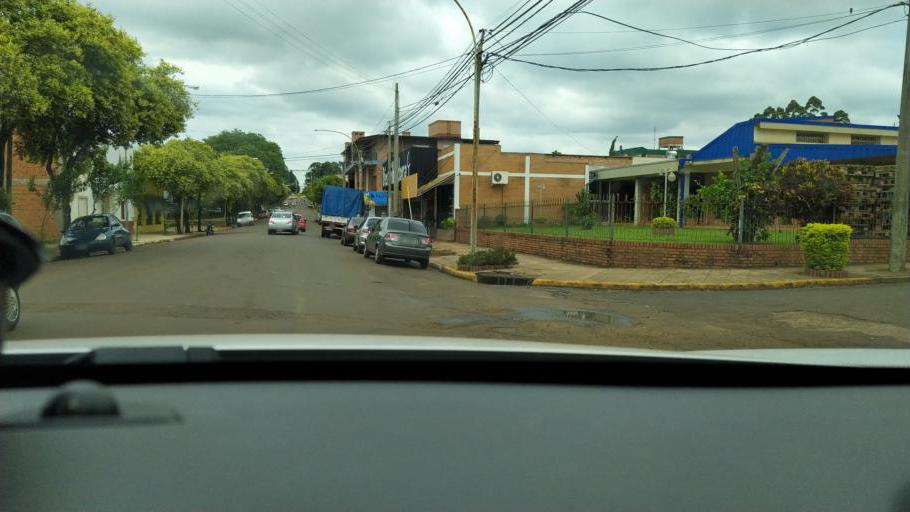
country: AR
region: Misiones
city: Puerto Rico
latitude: -26.8171
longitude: -55.0223
